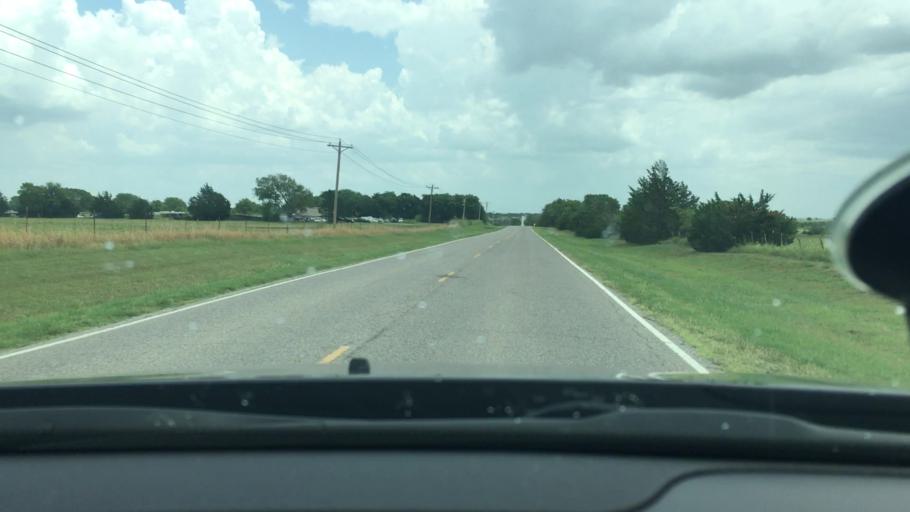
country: US
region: Oklahoma
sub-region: Love County
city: Marietta
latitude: 33.9403
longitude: -97.0506
